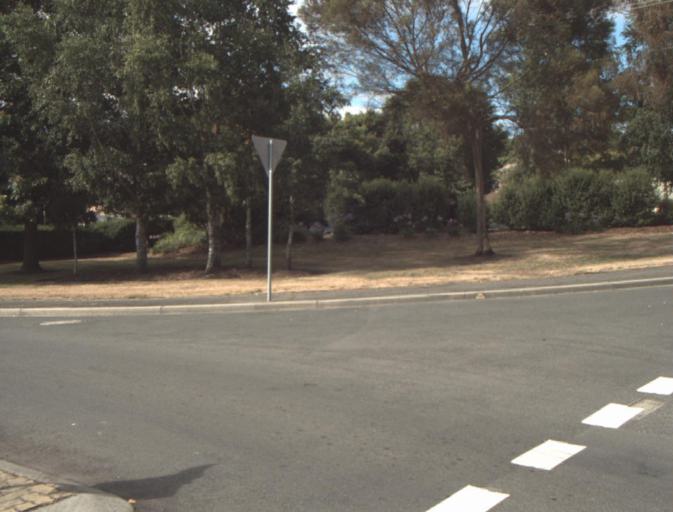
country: AU
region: Tasmania
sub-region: Launceston
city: Summerhill
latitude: -41.4633
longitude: 147.1230
